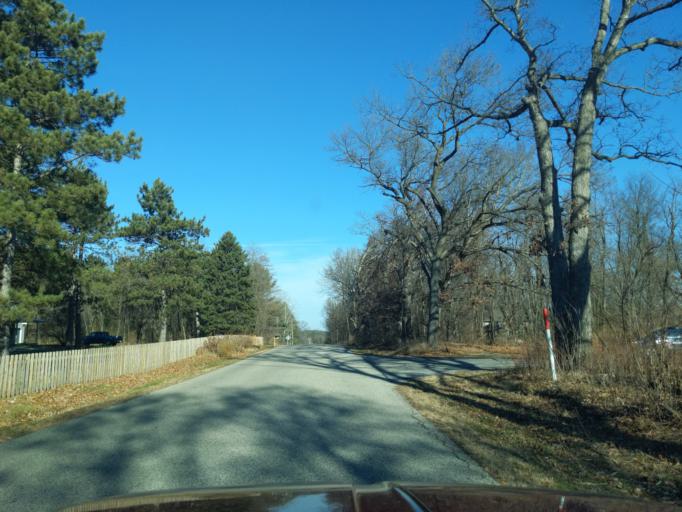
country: US
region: Wisconsin
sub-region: Waushara County
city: Silver Lake
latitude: 44.0566
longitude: -89.1886
